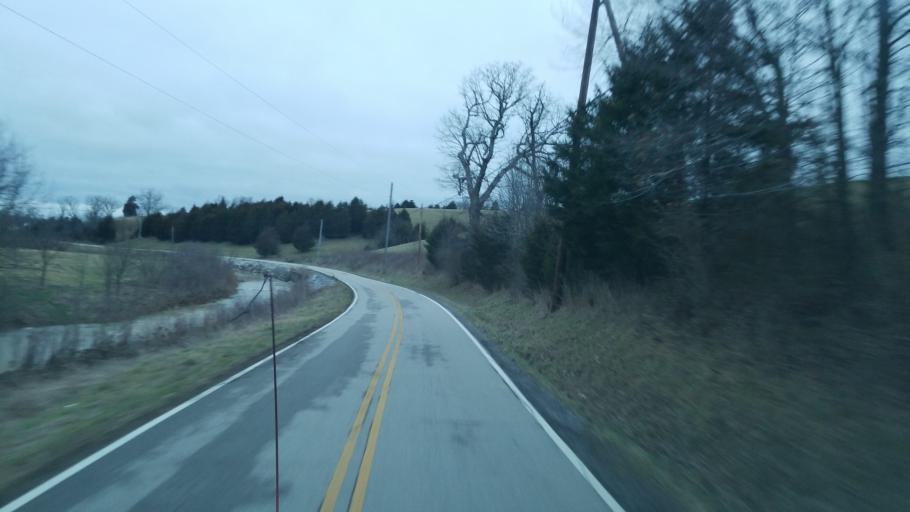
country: US
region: Kentucky
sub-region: Mason County
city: Maysville
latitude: 38.5415
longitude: -83.6942
